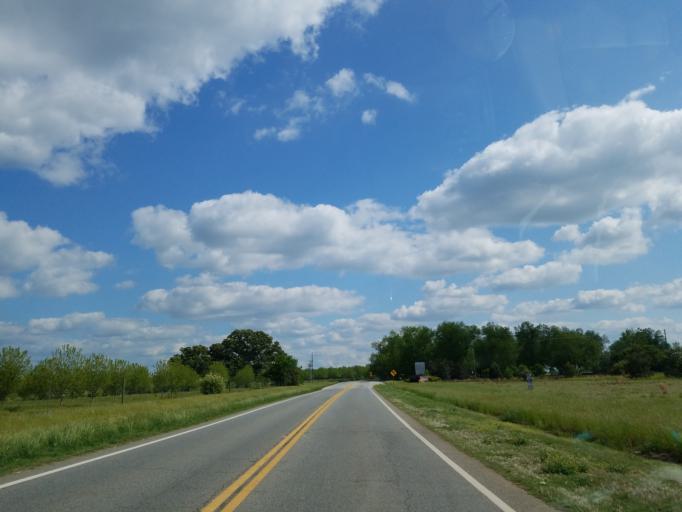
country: US
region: Georgia
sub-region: Peach County
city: Fort Valley
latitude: 32.5233
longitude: -83.8648
